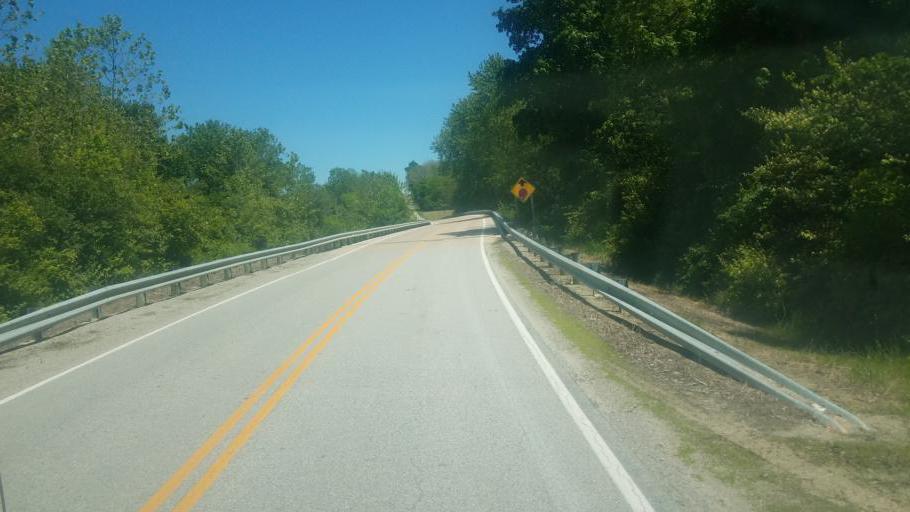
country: US
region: Ohio
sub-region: Miami County
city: Piqua
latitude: 40.2100
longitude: -84.2165
